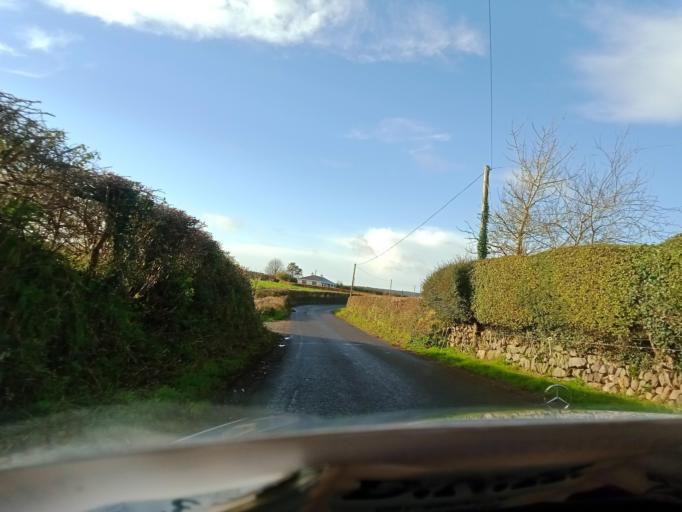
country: IE
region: Leinster
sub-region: Kilkenny
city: Mooncoin
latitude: 52.2808
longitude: -7.2077
